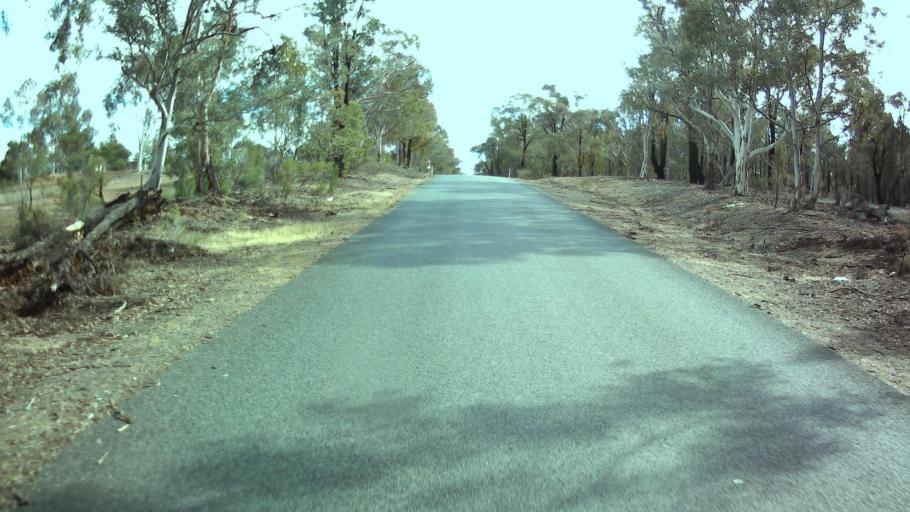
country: AU
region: New South Wales
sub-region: Weddin
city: Grenfell
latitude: -33.8877
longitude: 148.1960
